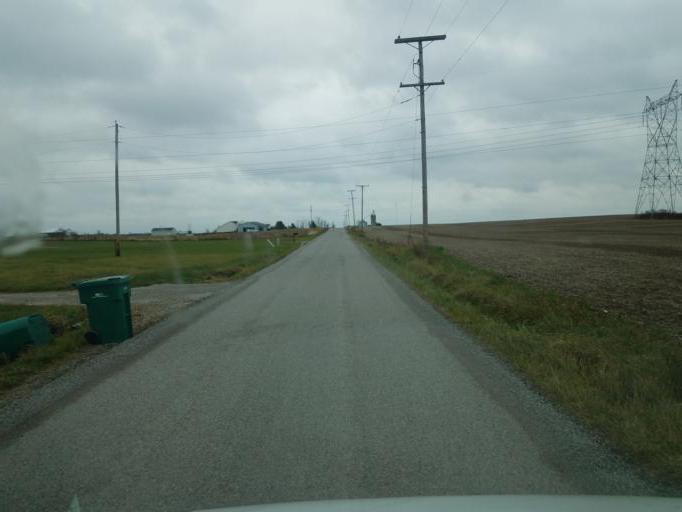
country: US
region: Ohio
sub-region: Knox County
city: Centerburg
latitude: 40.2575
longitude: -82.6407
